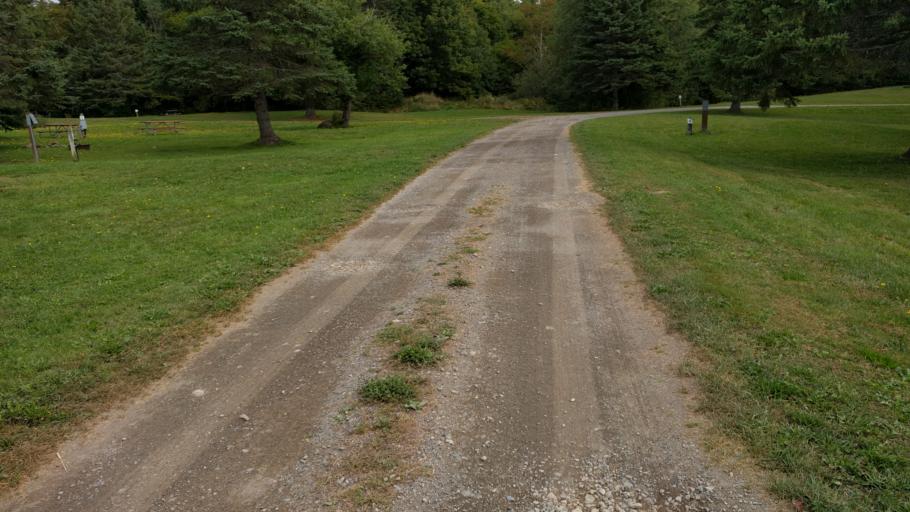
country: US
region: Maine
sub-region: Penobscot County
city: Patten
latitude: 46.1070
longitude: -68.5593
